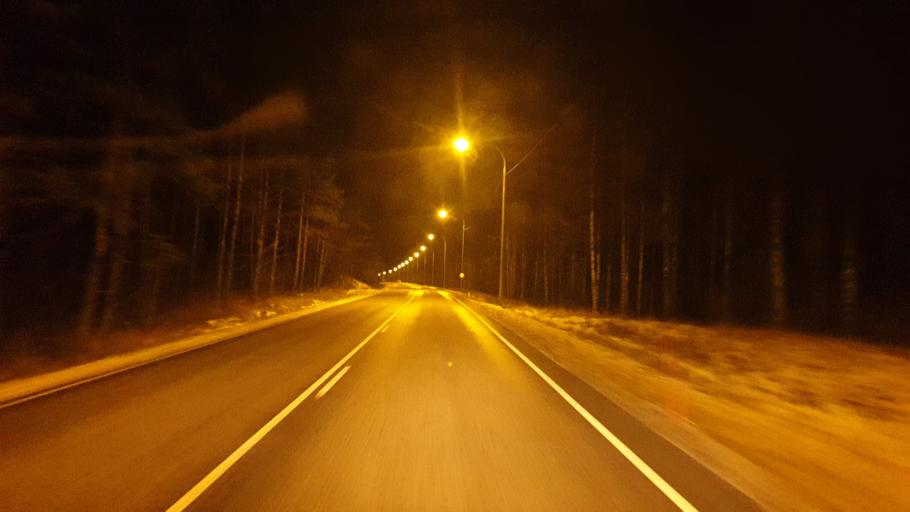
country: FI
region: Northern Savo
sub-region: Sisae-Savo
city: Suonenjoki
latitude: 62.6769
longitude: 27.4042
